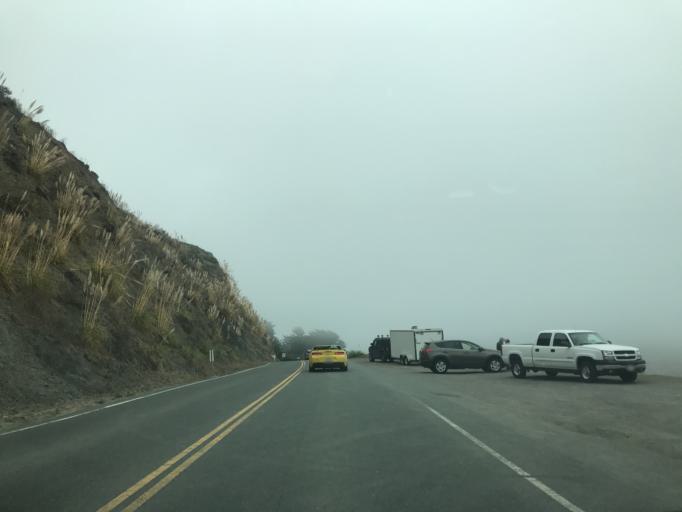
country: US
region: California
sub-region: Sonoma County
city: Monte Rio
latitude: 38.4528
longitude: -123.1287
